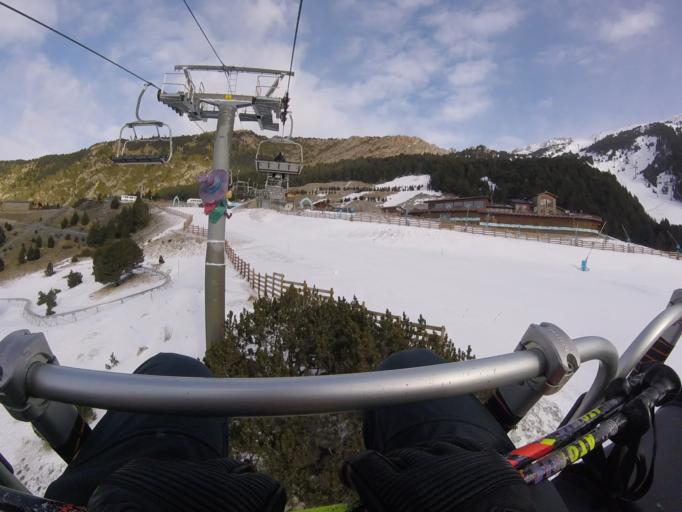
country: AD
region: Canillo
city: Canillo
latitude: 42.5547
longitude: 1.6148
